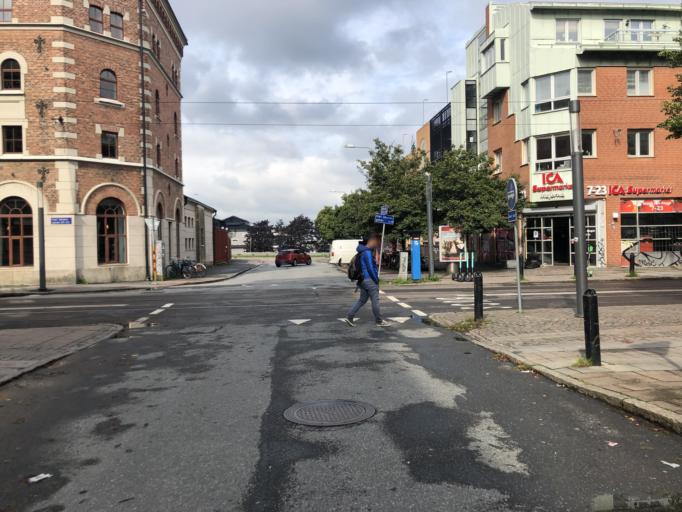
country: SE
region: Vaestra Goetaland
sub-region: Goteborg
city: Majorna
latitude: 57.6968
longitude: 11.9274
